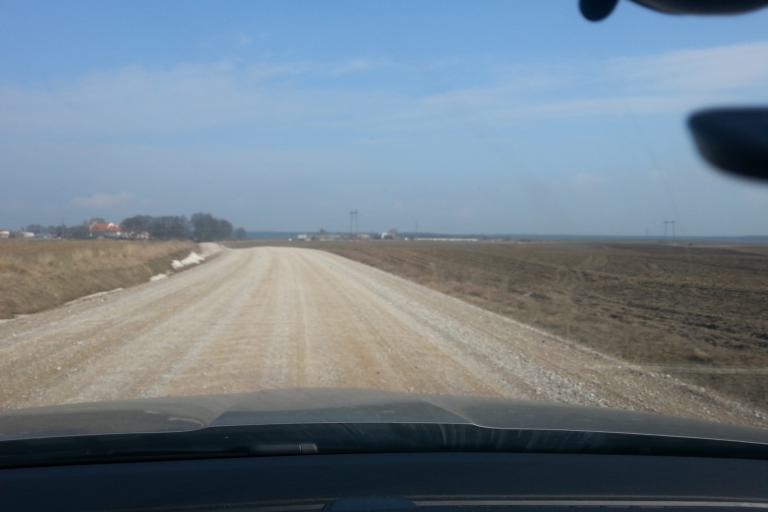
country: LT
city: Trakai
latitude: 54.5995
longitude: 24.9801
